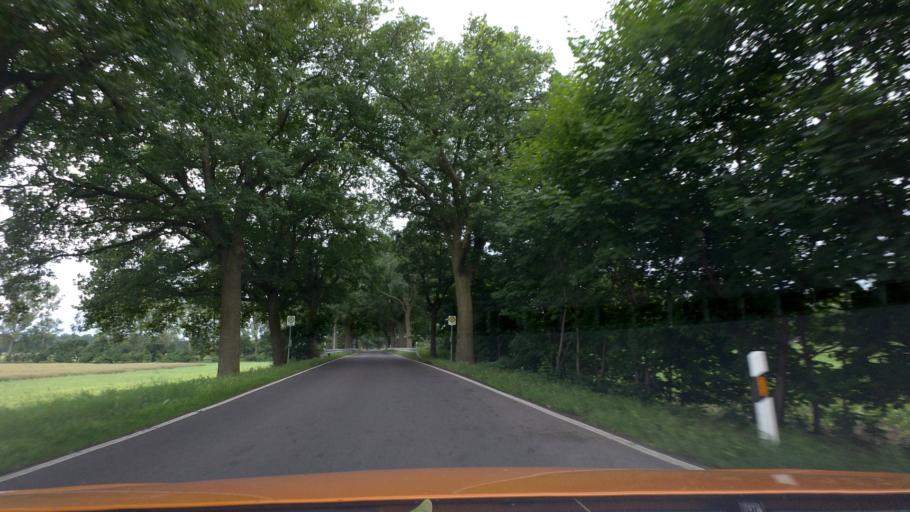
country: DE
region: Brandenburg
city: Neulewin
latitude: 52.7419
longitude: 14.2447
